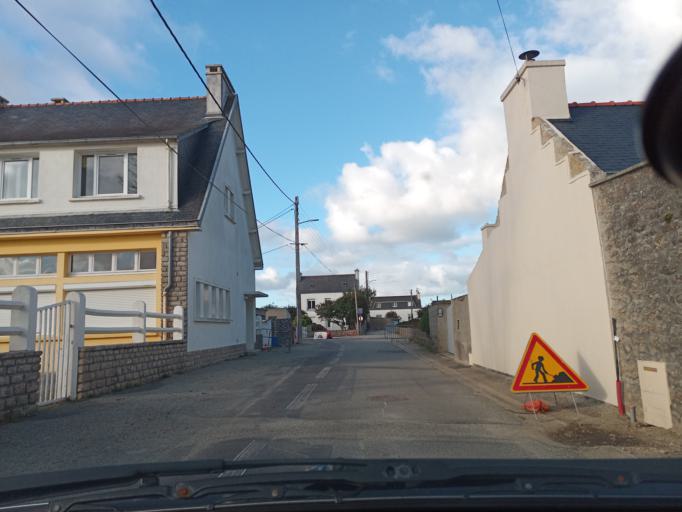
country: FR
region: Brittany
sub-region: Departement du Finistere
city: Plouhinec
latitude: 48.0155
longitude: -4.4909
